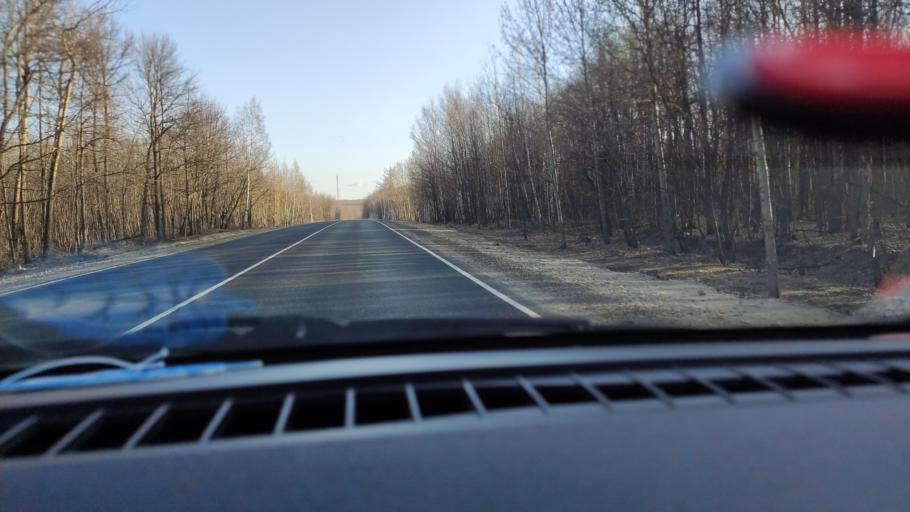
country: RU
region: Saratov
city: Khvalynsk
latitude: 52.4543
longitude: 48.0140
